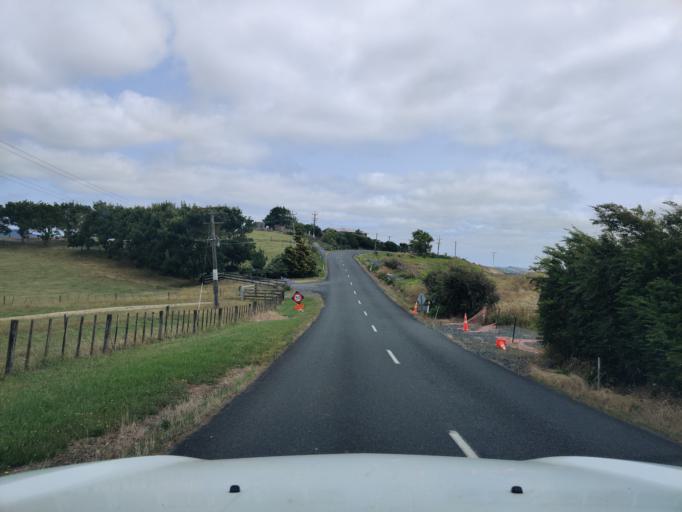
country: NZ
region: Waikato
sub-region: Waikato District
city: Te Kauwhata
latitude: -37.5207
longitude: 175.1771
